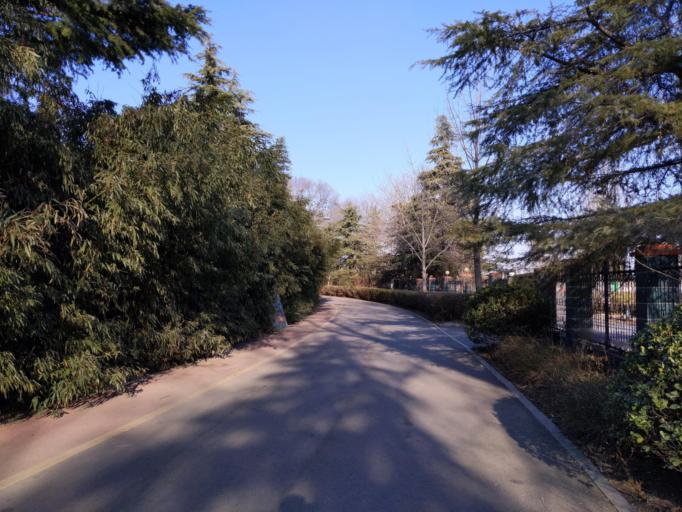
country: CN
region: Henan Sheng
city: Puyang
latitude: 35.7756
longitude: 114.9630
